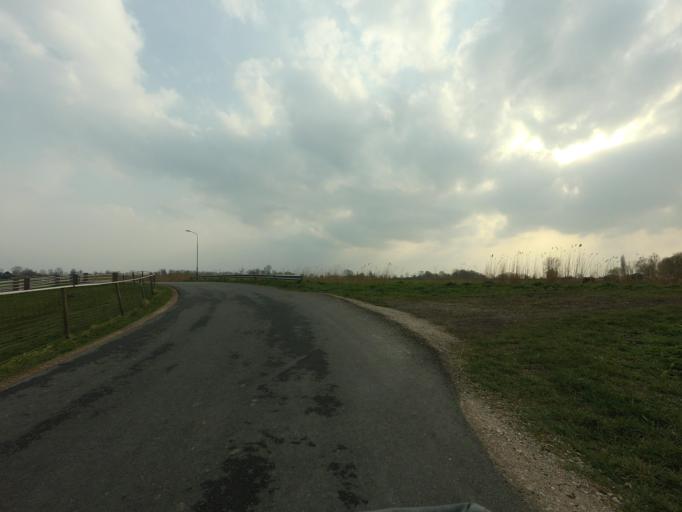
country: NL
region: Utrecht
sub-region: Gemeente De Ronde Venen
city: Mijdrecht
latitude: 52.1888
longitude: 4.8378
